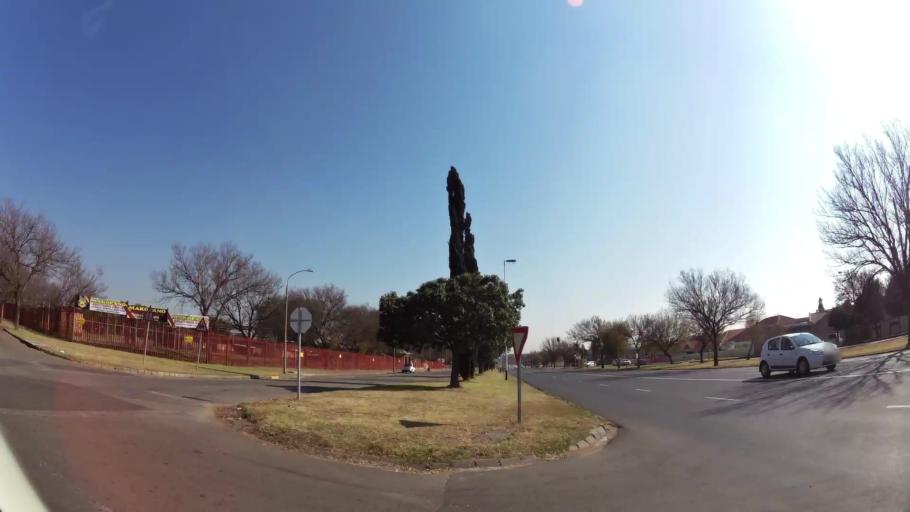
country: ZA
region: Gauteng
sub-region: Ekurhuleni Metropolitan Municipality
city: Boksburg
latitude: -26.2432
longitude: 28.2667
